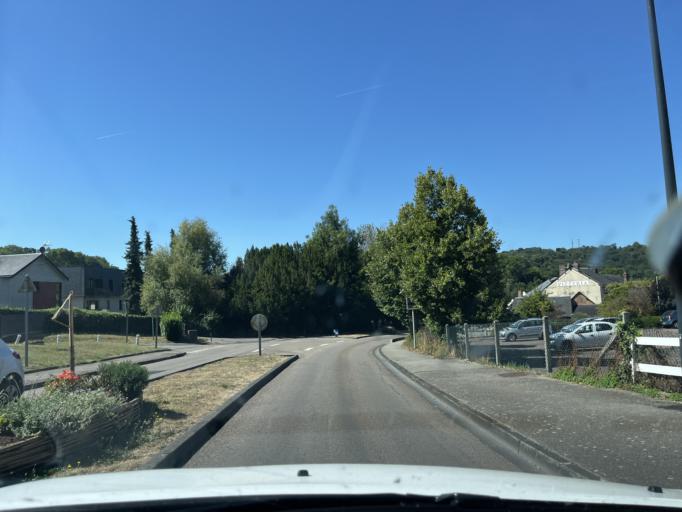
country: FR
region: Haute-Normandie
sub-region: Departement de la Seine-Maritime
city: Lillebonne
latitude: 49.5184
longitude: 0.5432
